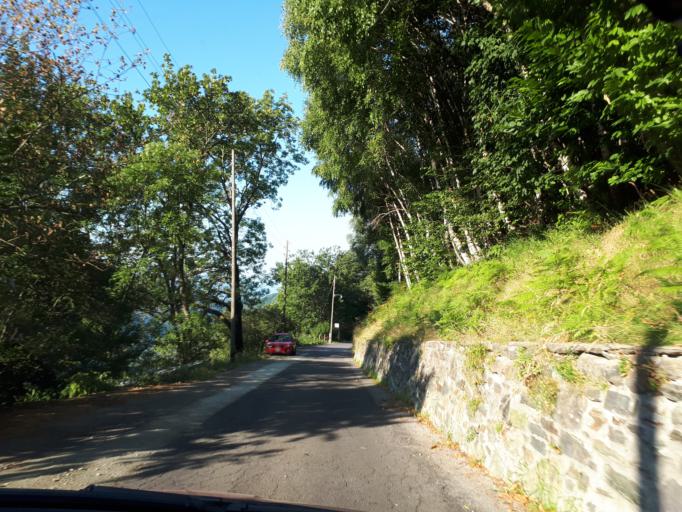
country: IT
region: Lombardy
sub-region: Provincia di Varese
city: Veddasca
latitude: 46.0994
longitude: 8.8336
